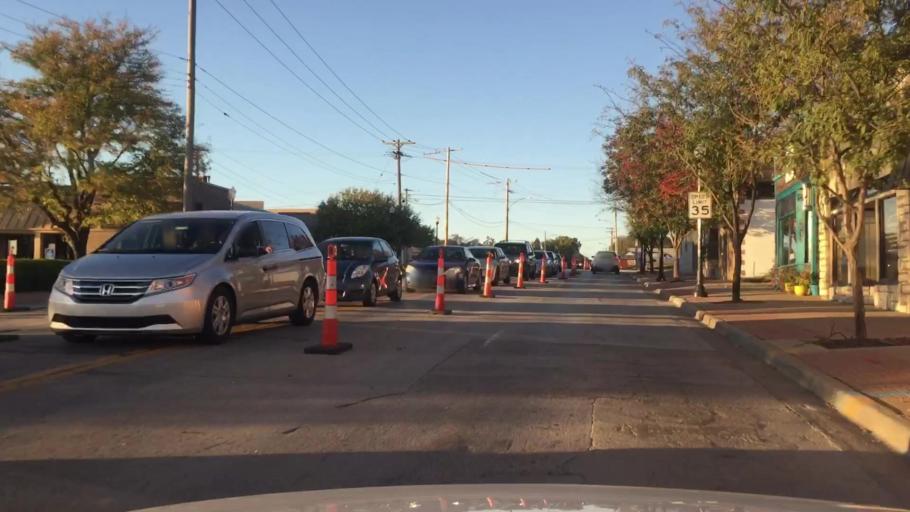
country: US
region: Kansas
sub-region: Johnson County
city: Shawnee
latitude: 39.0232
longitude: -94.7146
